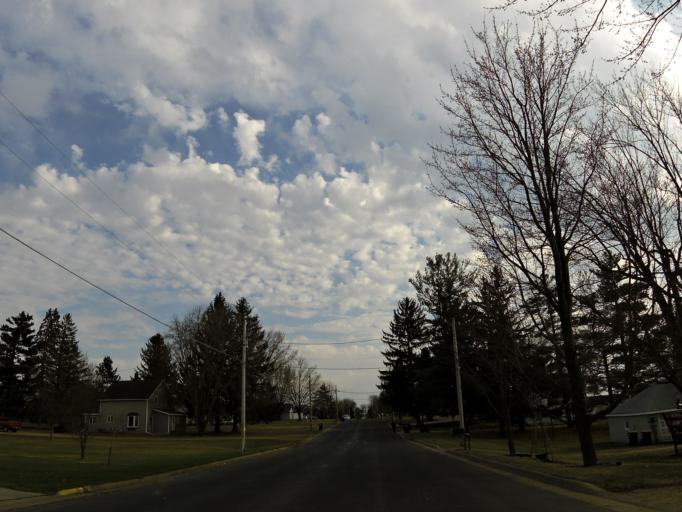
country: US
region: Wisconsin
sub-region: Pierce County
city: Ellsworth
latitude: 44.7211
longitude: -92.4797
